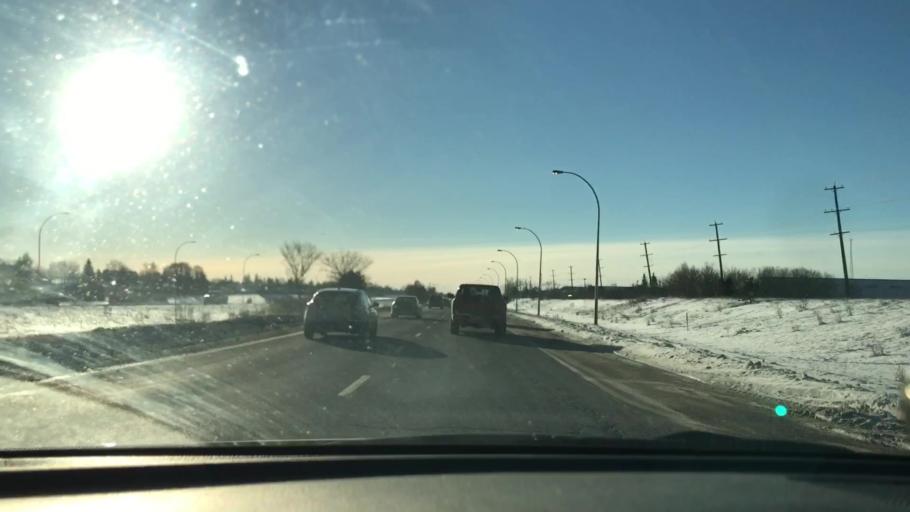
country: CA
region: Alberta
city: Edmonton
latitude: 53.4812
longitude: -113.4672
